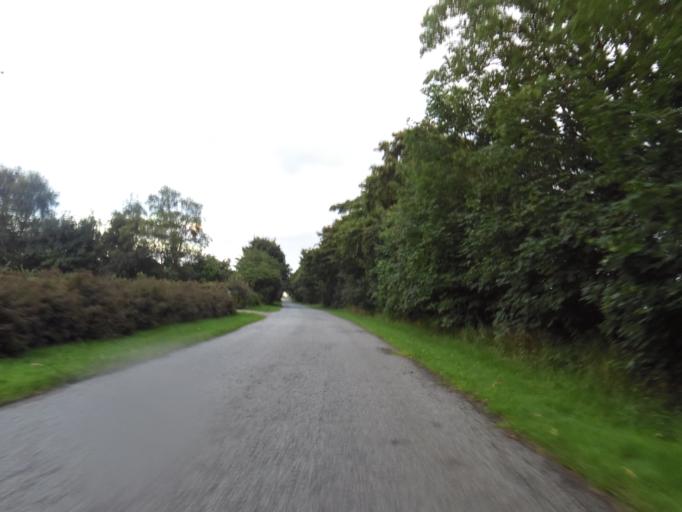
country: DK
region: South Denmark
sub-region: Esbjerg Kommune
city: Ribe
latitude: 55.2787
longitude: 8.8172
